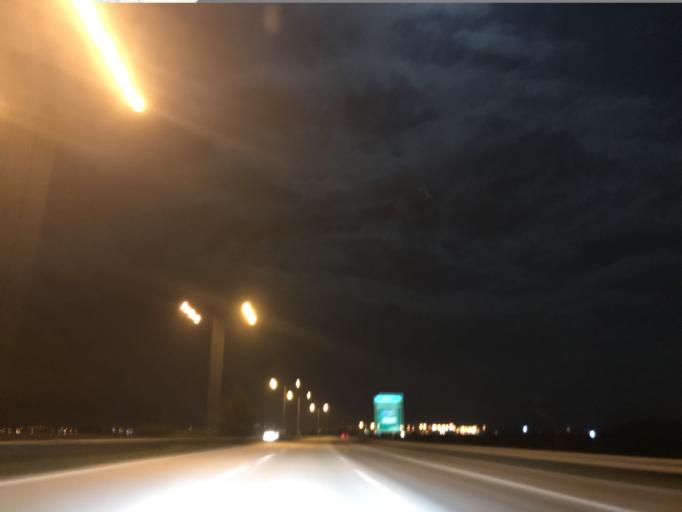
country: TR
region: Hatay
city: Mahmutlar
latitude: 36.9579
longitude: 36.1452
